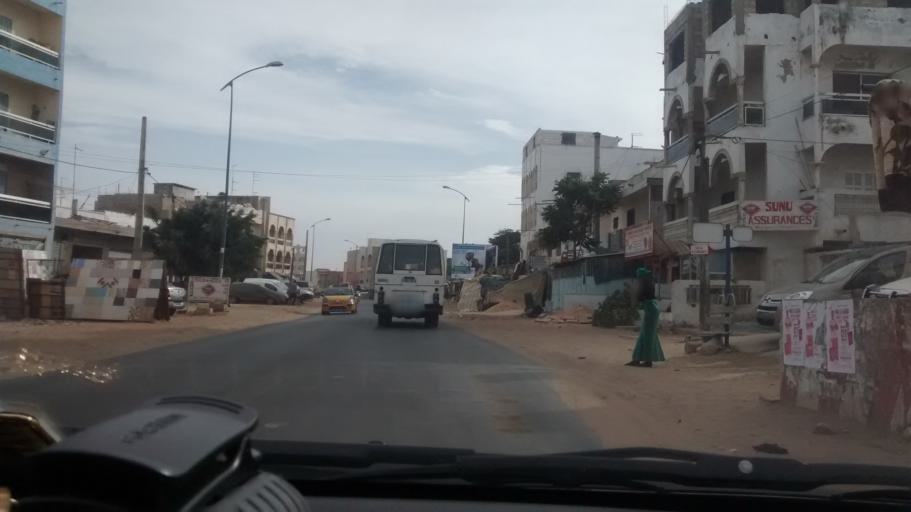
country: SN
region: Dakar
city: Pikine
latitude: 14.7653
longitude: -17.4172
